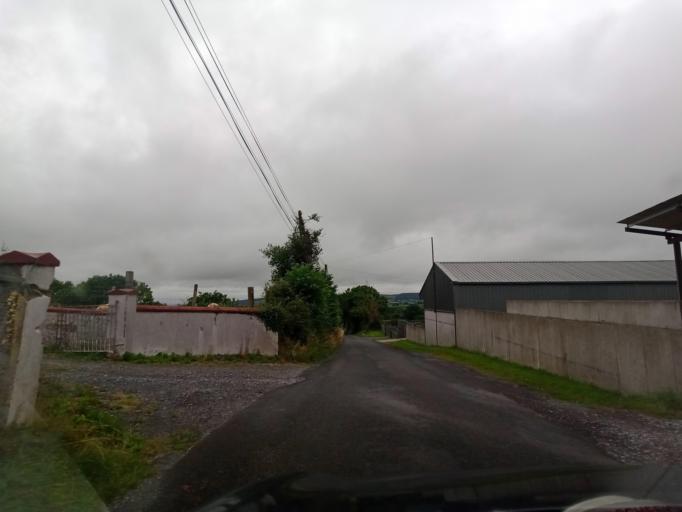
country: IE
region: Leinster
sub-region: Laois
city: Stradbally
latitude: 52.9539
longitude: -7.2207
